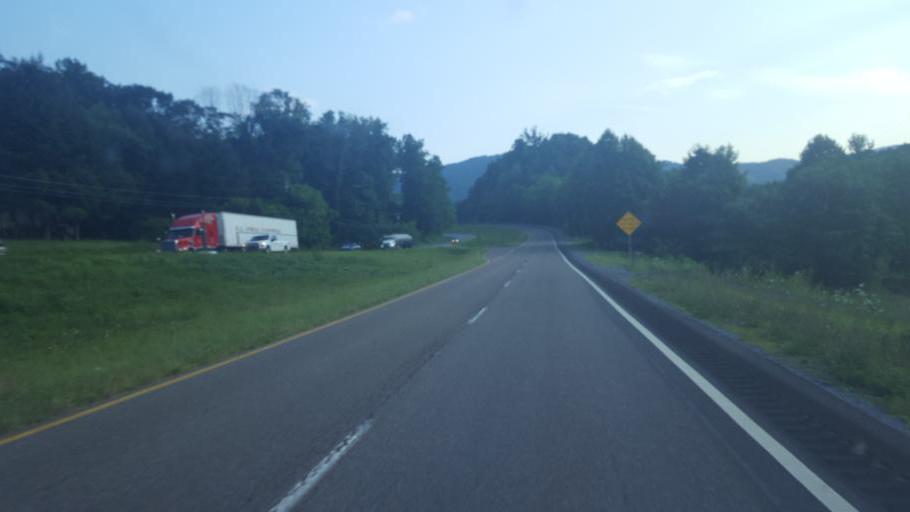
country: US
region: Virginia
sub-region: Lee County
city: Dryden
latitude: 36.7808
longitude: -82.8202
